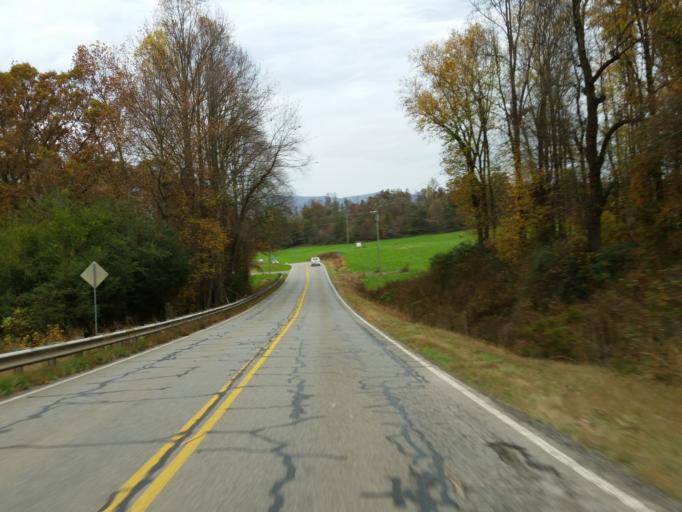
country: US
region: Georgia
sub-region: Gilmer County
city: Ellijay
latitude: 34.6351
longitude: -84.3871
